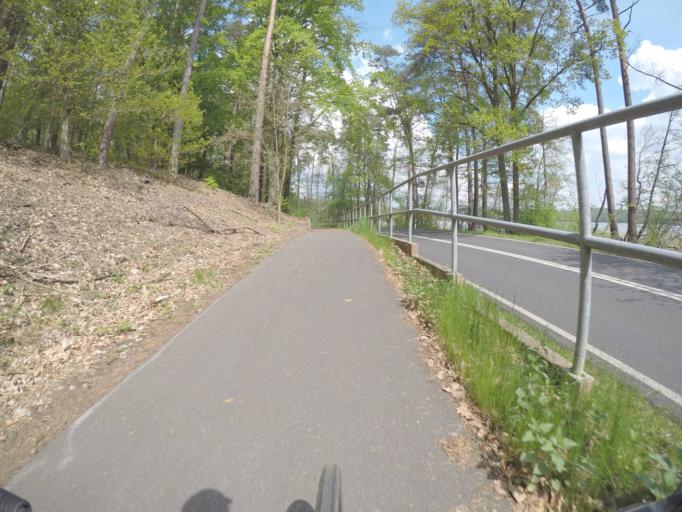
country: DE
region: Brandenburg
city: Joachimsthal
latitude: 52.9291
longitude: 13.7061
